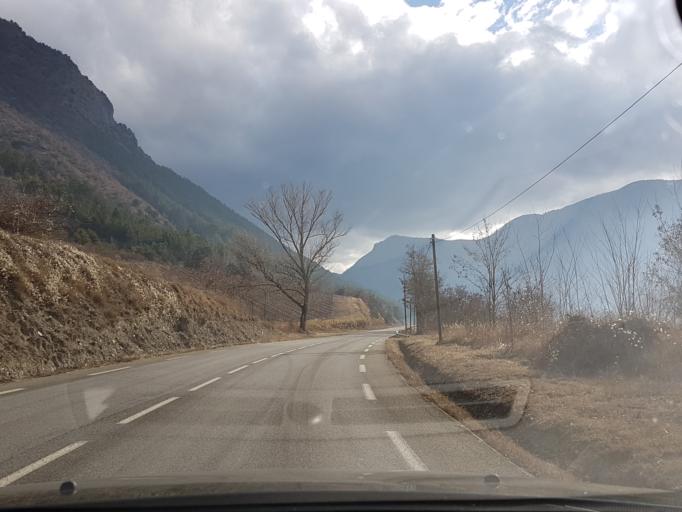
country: FR
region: Provence-Alpes-Cote d'Azur
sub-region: Departement des Hautes-Alpes
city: Tallard
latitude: 44.4760
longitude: 6.1212
